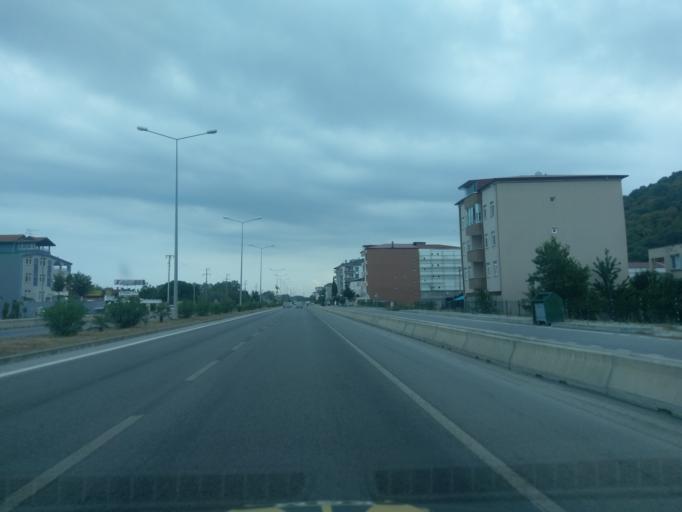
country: TR
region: Samsun
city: Taflan
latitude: 41.3859
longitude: 36.2081
